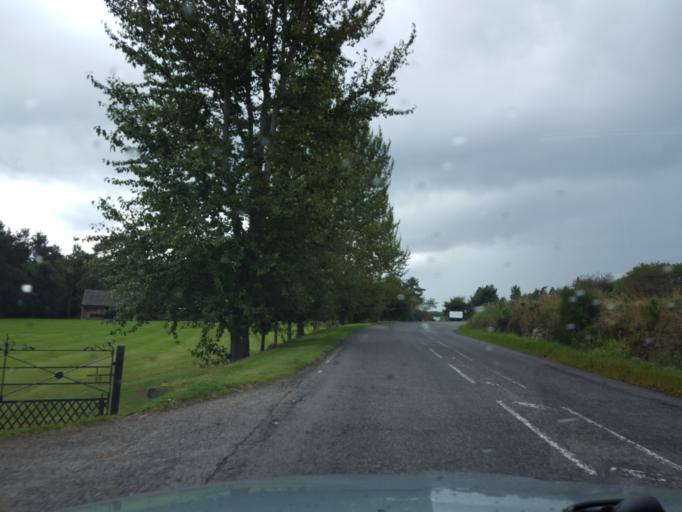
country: GB
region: Scotland
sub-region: Aberdeenshire
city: Torphins
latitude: 57.0865
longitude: -2.6810
